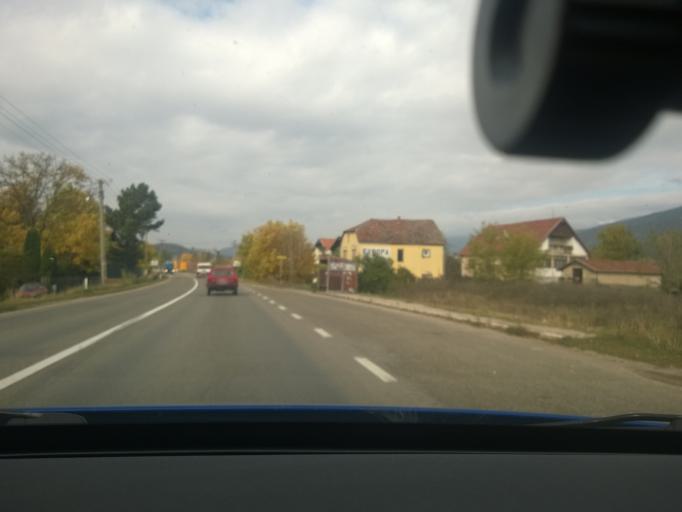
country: RS
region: Central Serbia
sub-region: Pirotski Okrug
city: Bela Palanka
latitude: 43.2697
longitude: 22.2418
